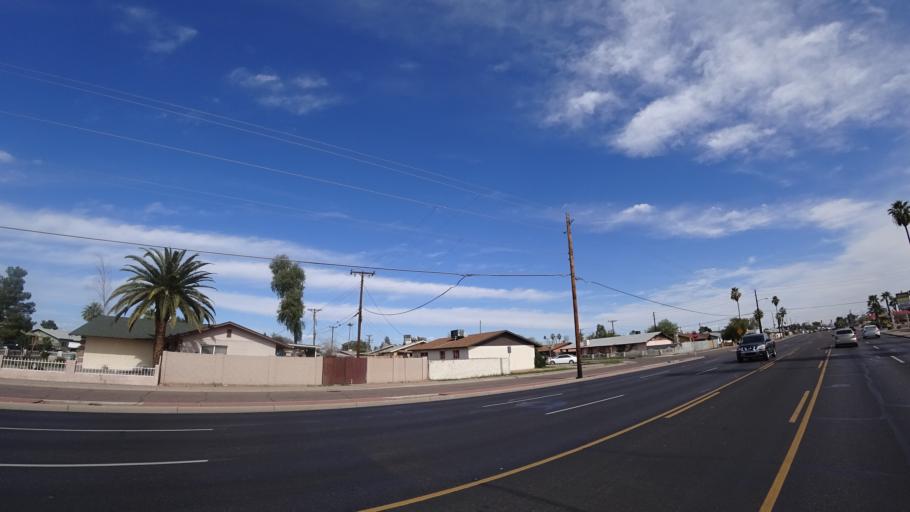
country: US
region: Arizona
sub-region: Maricopa County
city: Glendale
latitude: 33.4805
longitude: -112.1728
